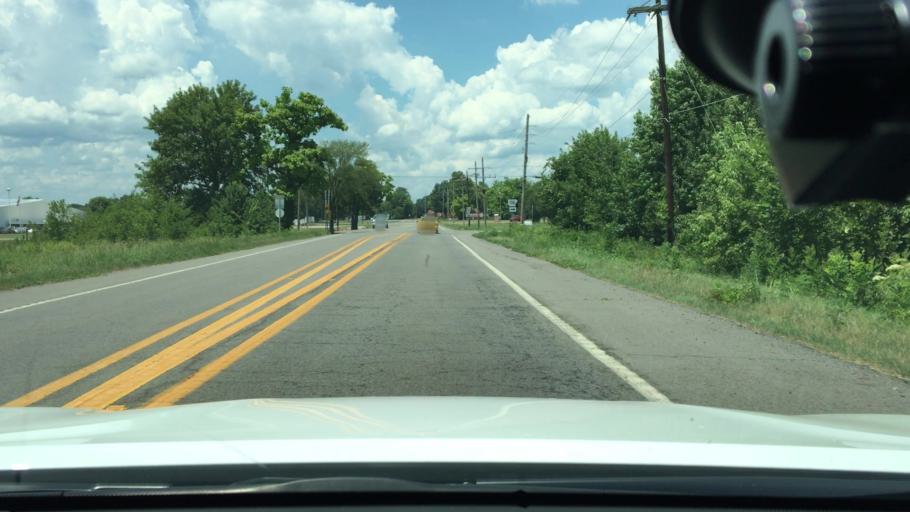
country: US
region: Arkansas
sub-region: Logan County
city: Booneville
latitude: 35.1480
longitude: -93.8763
